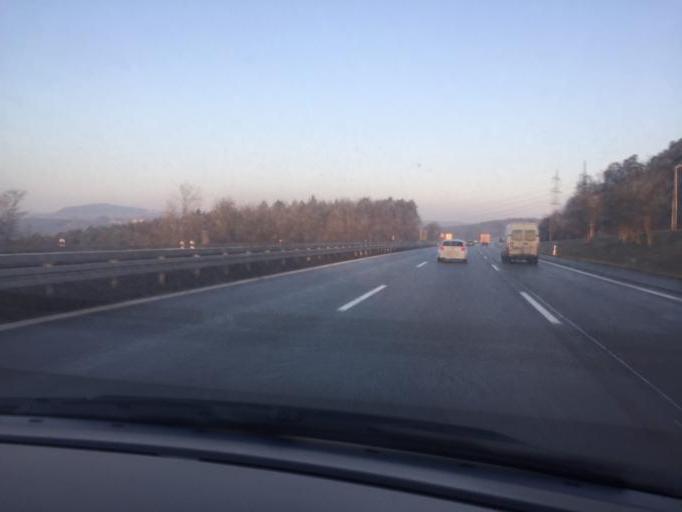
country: DE
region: Baden-Wuerttemberg
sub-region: Freiburg Region
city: Engen
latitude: 47.8640
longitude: 8.7846
